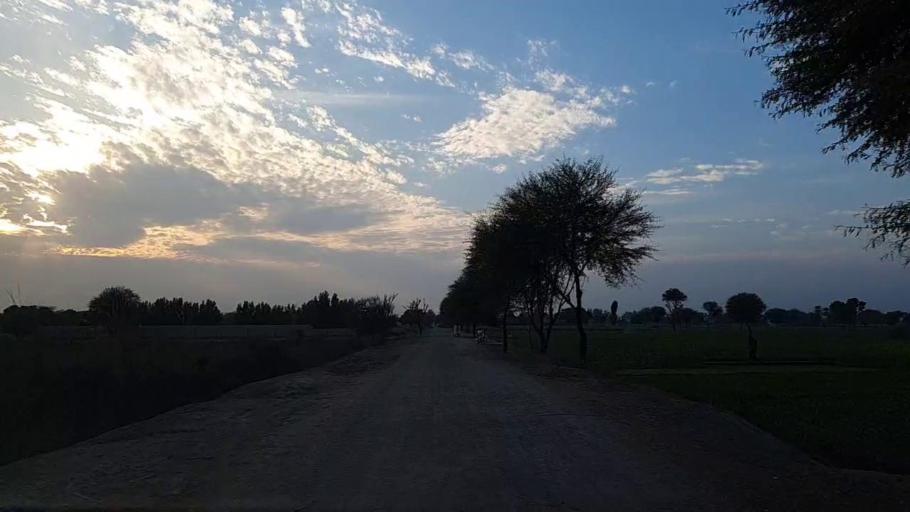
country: PK
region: Sindh
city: Daur
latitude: 26.4167
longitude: 68.4935
